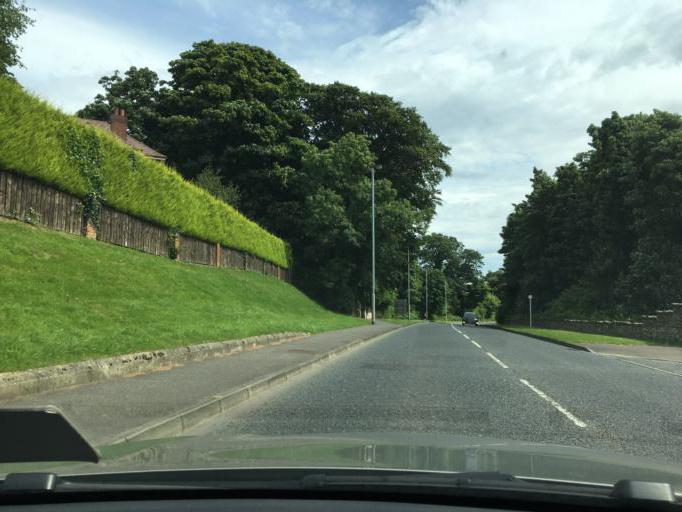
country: GB
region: Northern Ireland
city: Culmore
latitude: 55.0321
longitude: -7.2919
